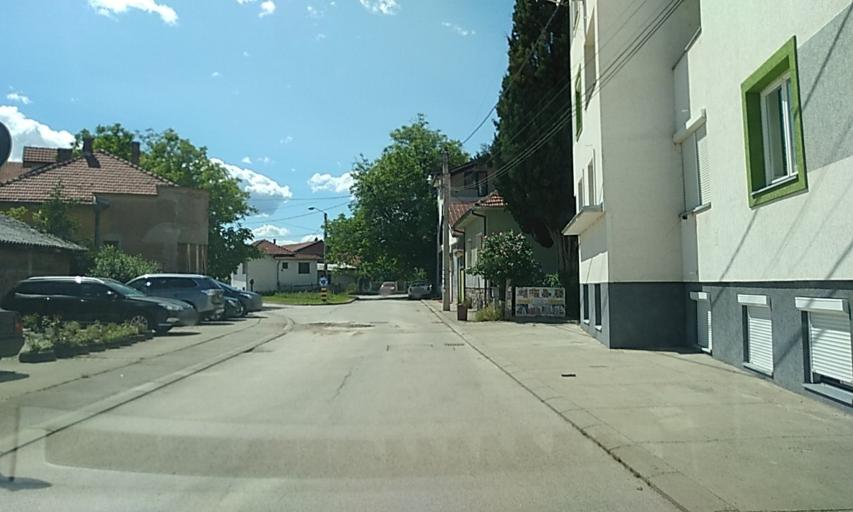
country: RS
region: Central Serbia
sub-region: Nisavski Okrug
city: Nis
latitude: 43.3296
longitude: 21.9061
